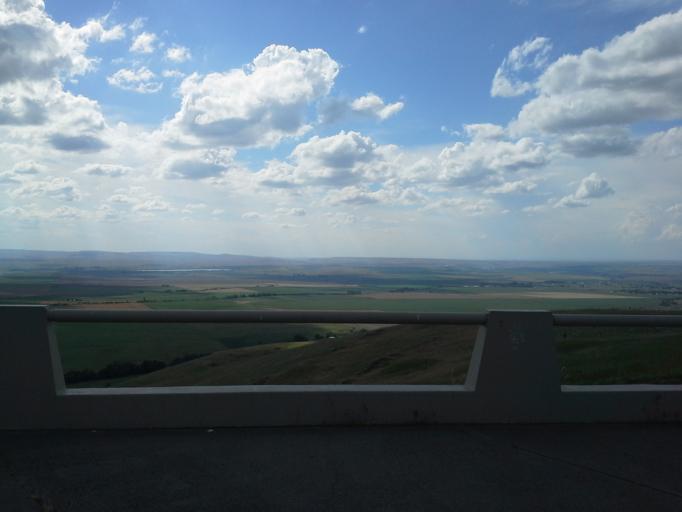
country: US
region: Oregon
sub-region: Umatilla County
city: Mission
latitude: 45.5815
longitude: -118.6443
